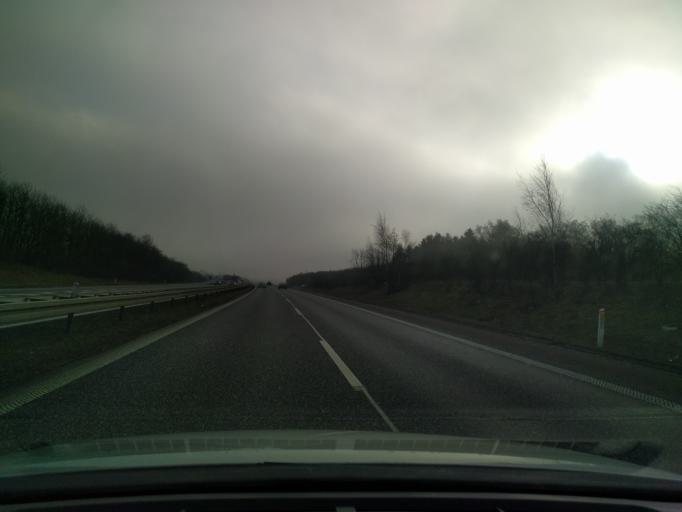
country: DK
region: Zealand
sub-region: Soro Kommune
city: Soro
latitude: 55.4581
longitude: 11.5777
